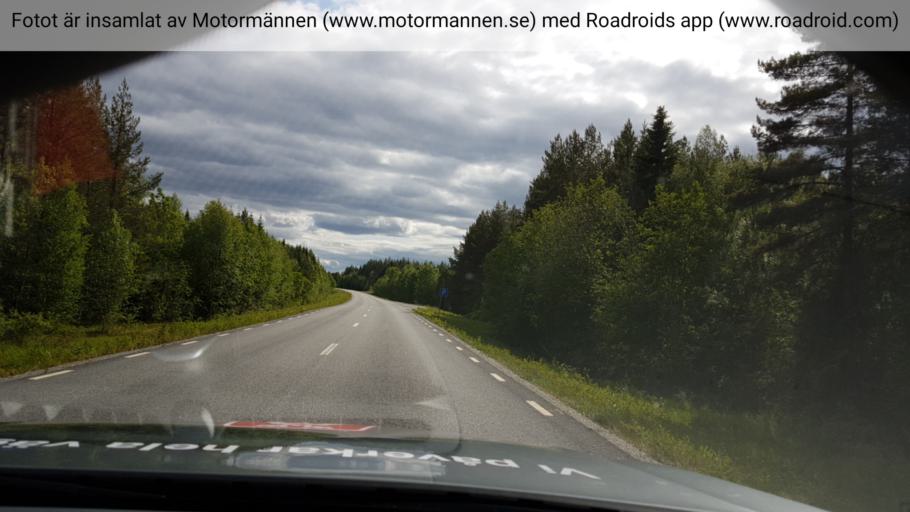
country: SE
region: Jaemtland
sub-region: Stroemsunds Kommun
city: Stroemsund
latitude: 64.0265
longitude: 15.5298
